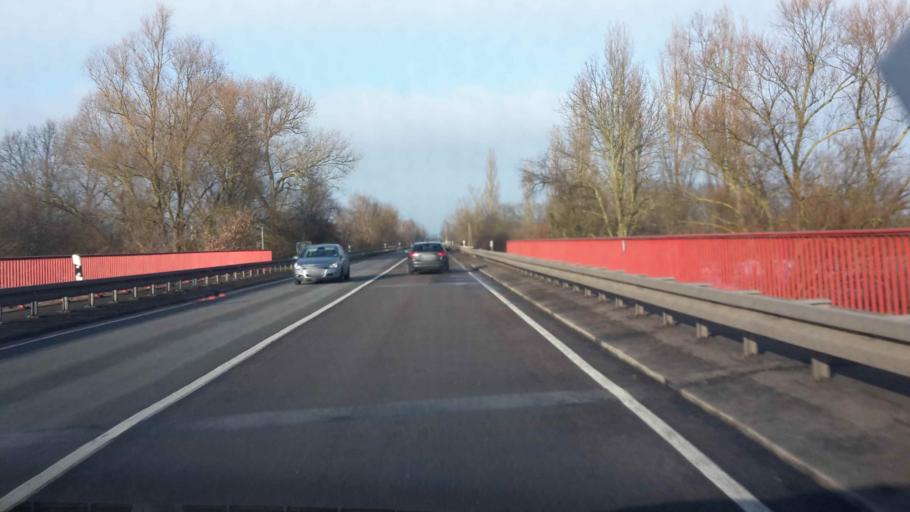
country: DE
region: Saxony-Anhalt
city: Seehausen
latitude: 52.9401
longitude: 11.7282
